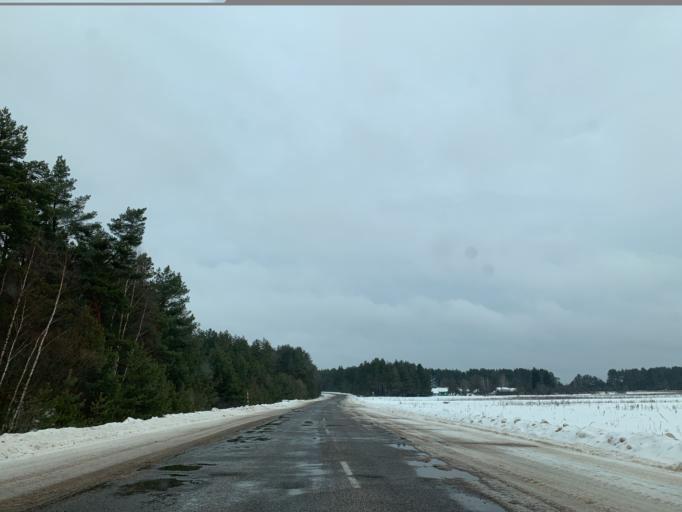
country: BY
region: Minsk
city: Il'ya
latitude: 54.3261
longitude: 27.2492
